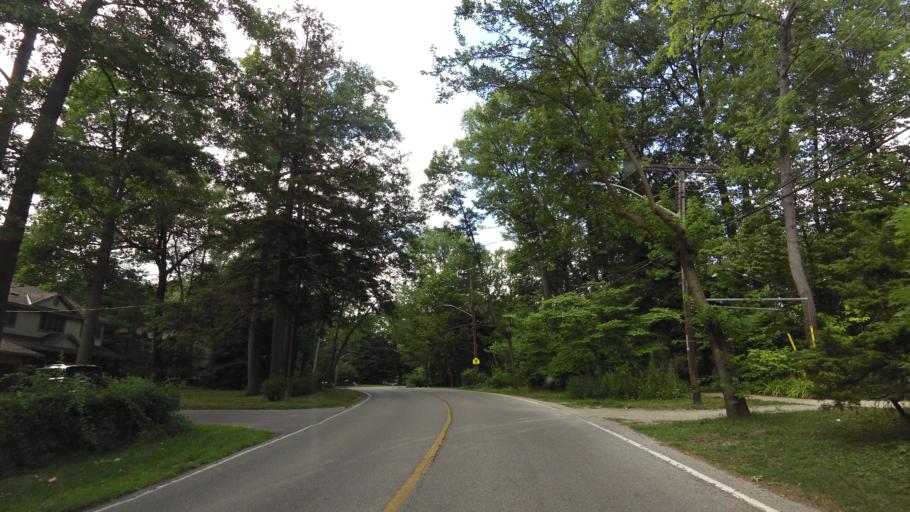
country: CA
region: Ontario
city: Mississauga
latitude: 43.5140
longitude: -79.6114
